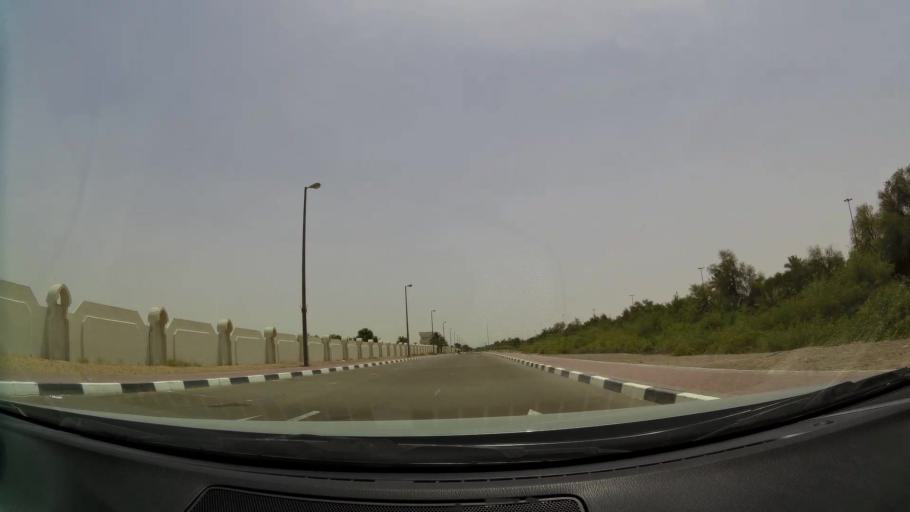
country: AE
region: Abu Dhabi
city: Al Ain
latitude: 24.1953
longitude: 55.6871
